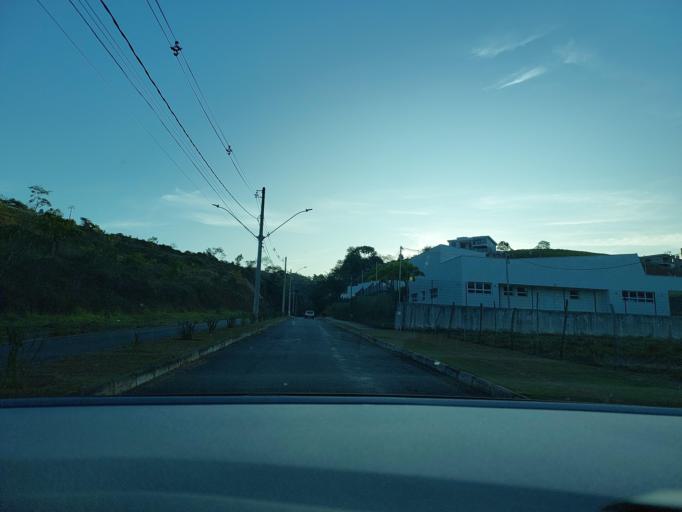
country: BR
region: Minas Gerais
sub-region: Vicosa
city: Vicosa
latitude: -20.7818
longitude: -42.8469
